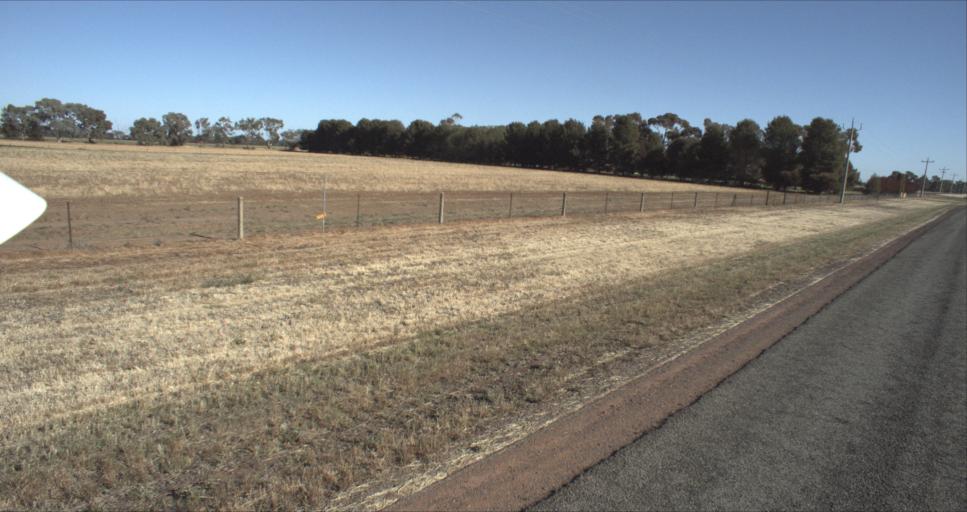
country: AU
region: New South Wales
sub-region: Leeton
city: Leeton
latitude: -34.5860
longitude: 146.2606
